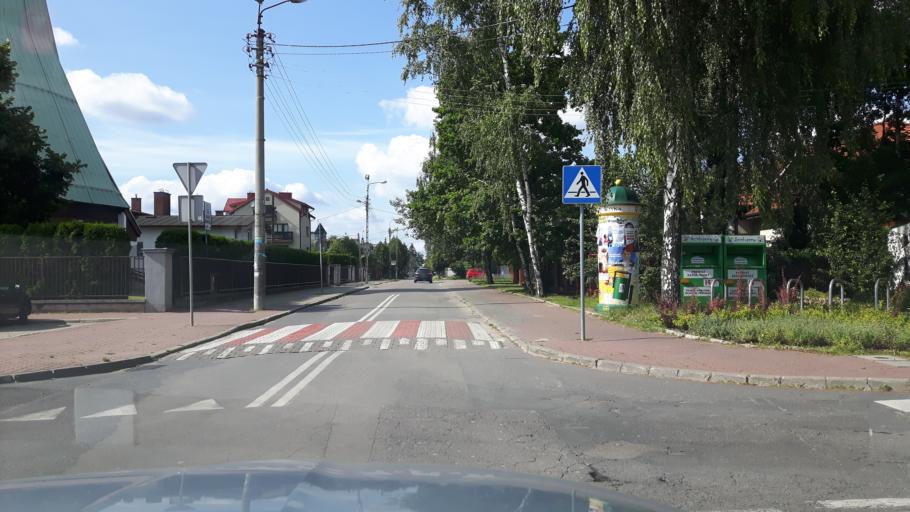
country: PL
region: Masovian Voivodeship
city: Zielonka
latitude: 52.2948
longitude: 21.1596
